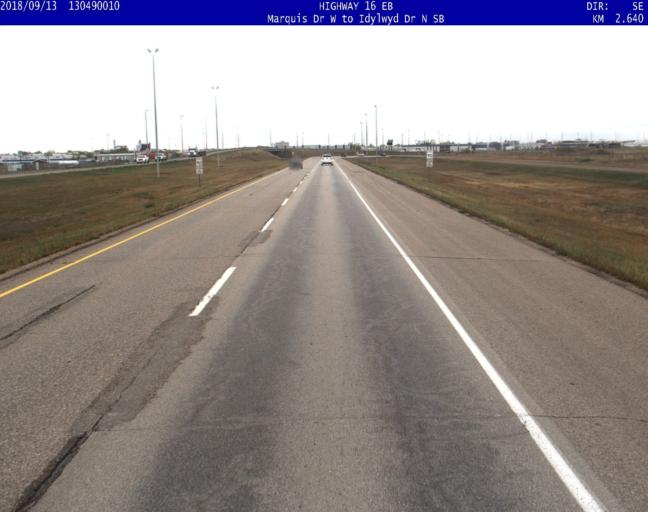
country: CA
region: Saskatchewan
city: Saskatoon
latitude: 52.1856
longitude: -106.6773
